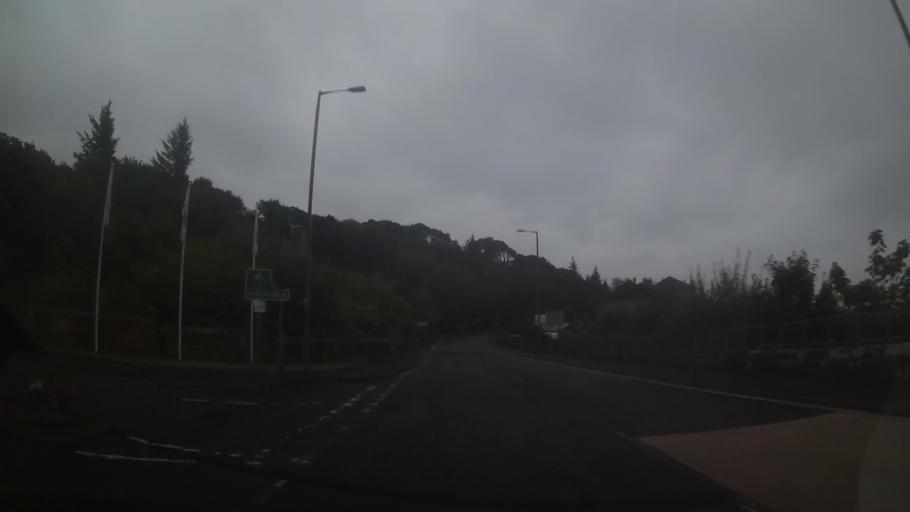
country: GB
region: Scotland
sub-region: Inverclyde
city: Wemyss Bay
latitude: 55.8754
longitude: -4.8891
